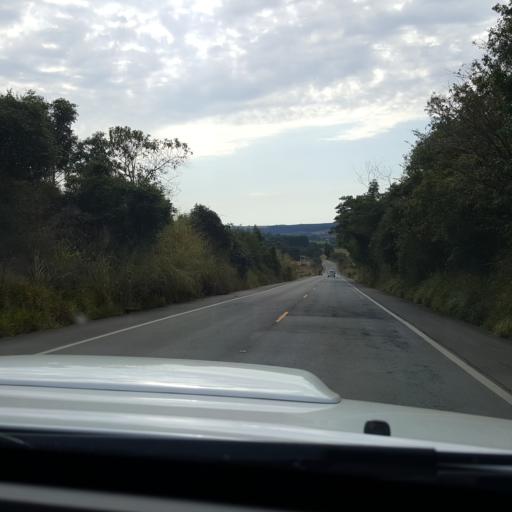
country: BR
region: Sao Paulo
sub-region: Itaporanga
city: Itaporanga
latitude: -23.7329
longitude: -49.4580
